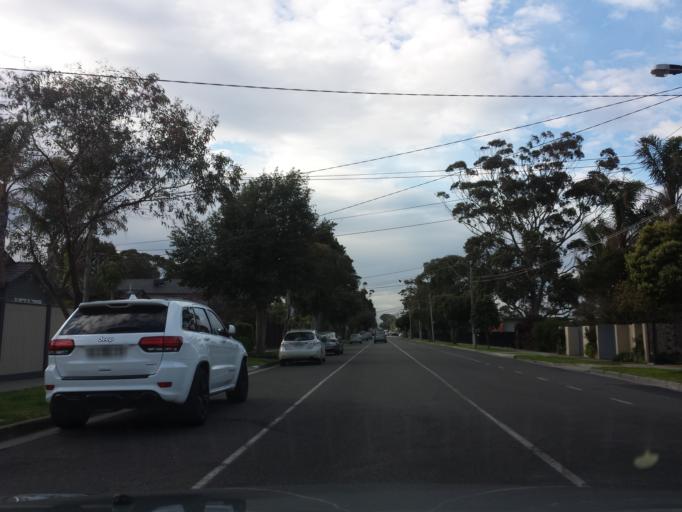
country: AU
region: Victoria
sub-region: Bayside
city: Cheltenham
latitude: -37.9824
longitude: 145.0526
